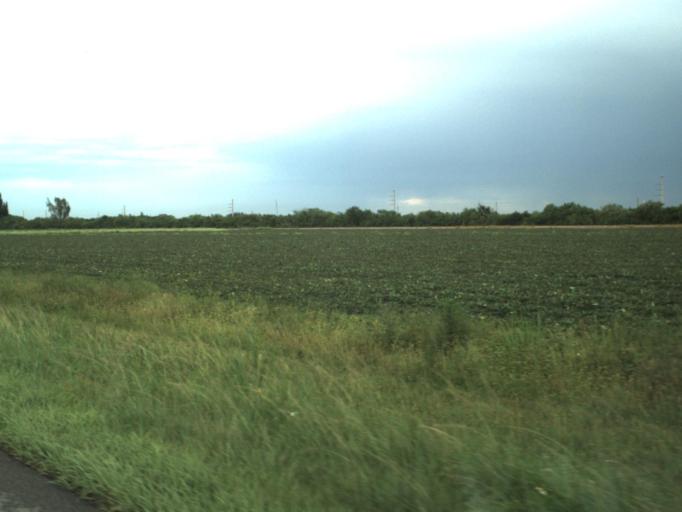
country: US
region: Florida
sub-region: Miami-Dade County
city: The Hammocks
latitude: 25.6734
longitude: -80.4813
